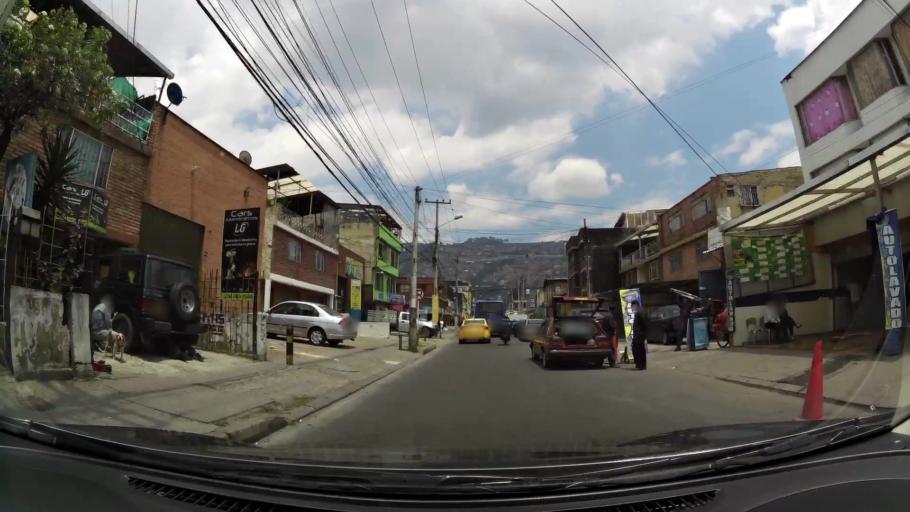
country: CO
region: Cundinamarca
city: La Calera
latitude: 4.7378
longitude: -74.0305
